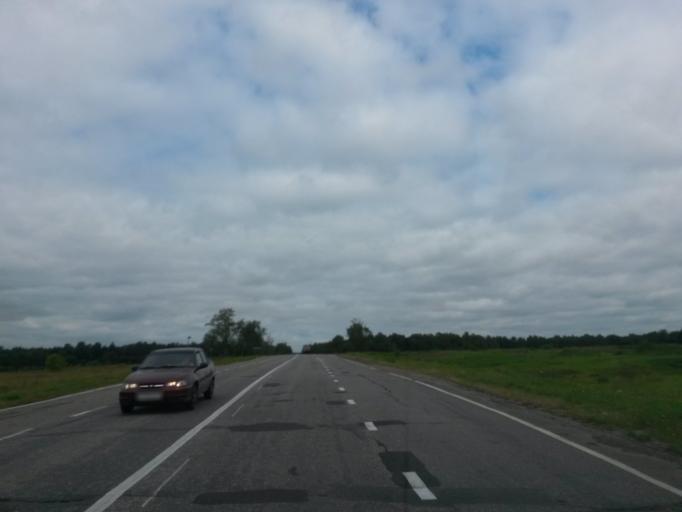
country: RU
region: Jaroslavl
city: Gavrilov-Yam
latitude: 57.4459
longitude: 39.9152
